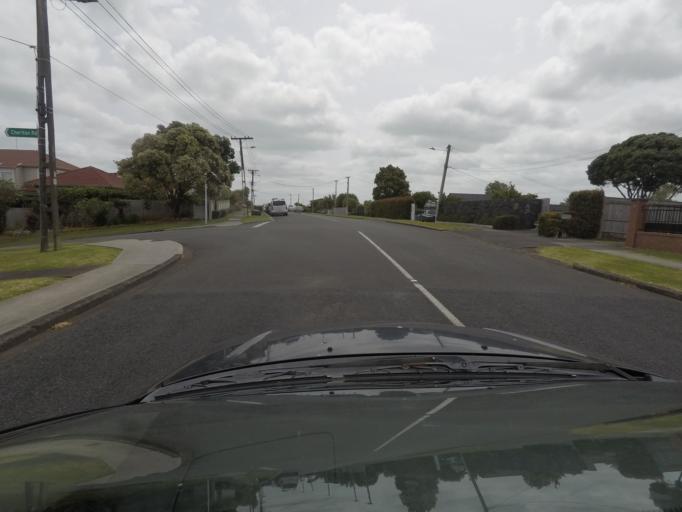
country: NZ
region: Auckland
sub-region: Auckland
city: Pakuranga
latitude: -36.8907
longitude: 174.9300
